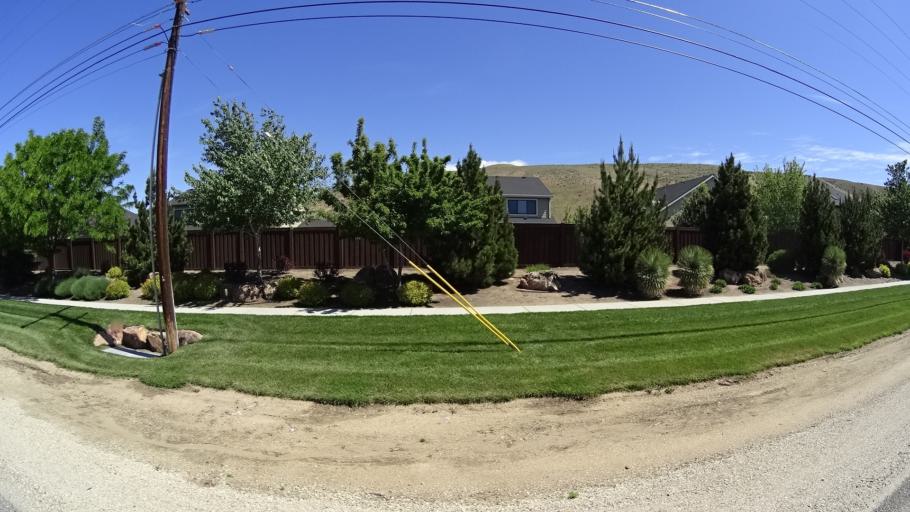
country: US
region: Idaho
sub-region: Ada County
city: Boise
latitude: 43.5636
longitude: -116.1096
